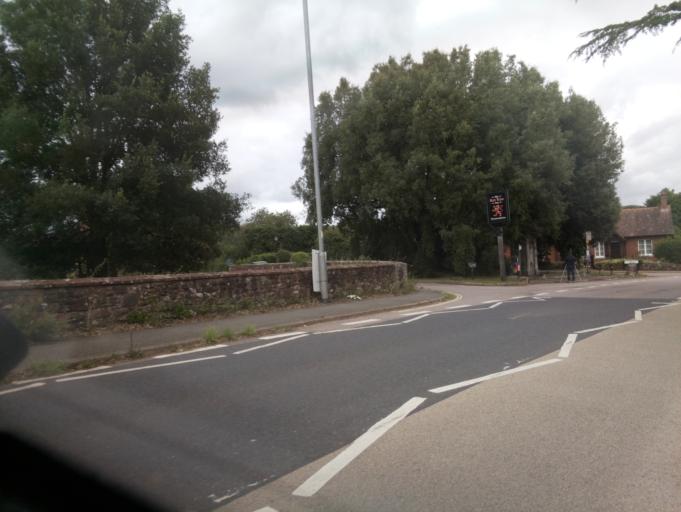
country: GB
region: England
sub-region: Devon
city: Heavitree
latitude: 50.7658
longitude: -3.4437
